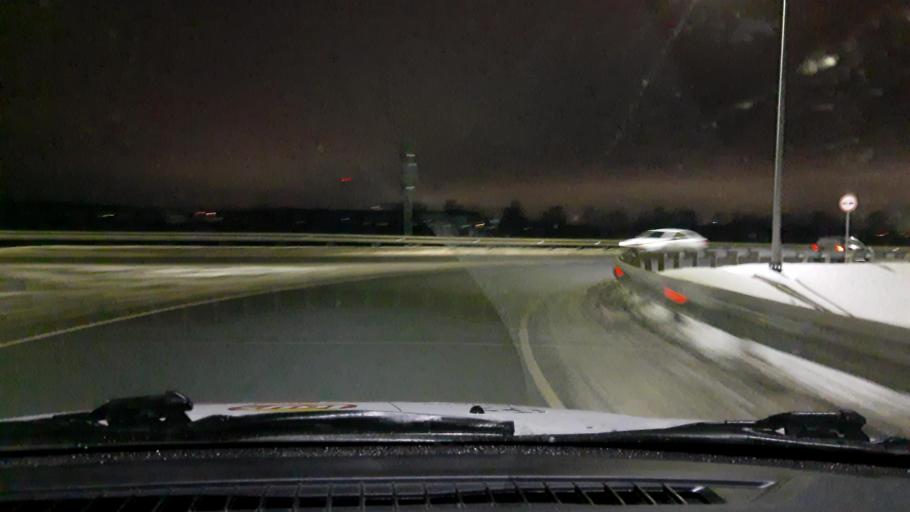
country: RU
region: Nizjnij Novgorod
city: Neklyudovo
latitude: 56.4218
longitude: 43.9900
